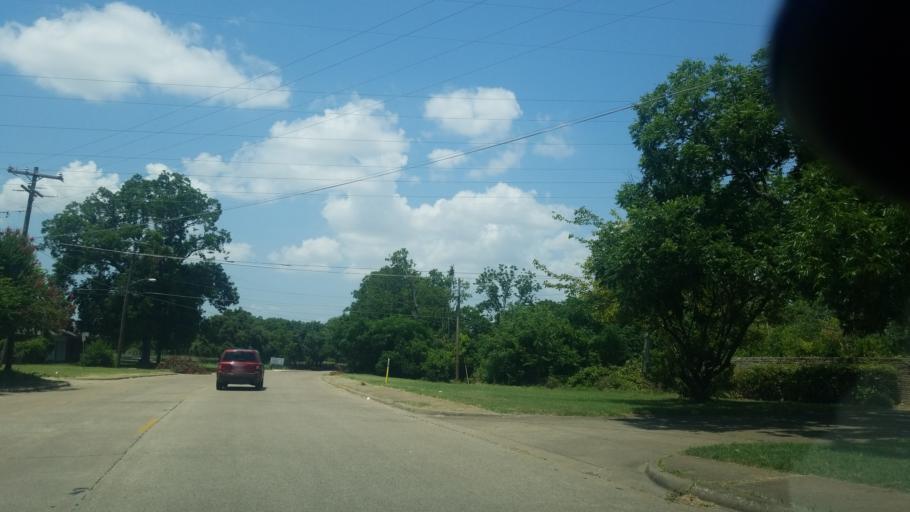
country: US
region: Texas
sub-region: Dallas County
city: Dallas
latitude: 32.7214
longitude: -96.7864
